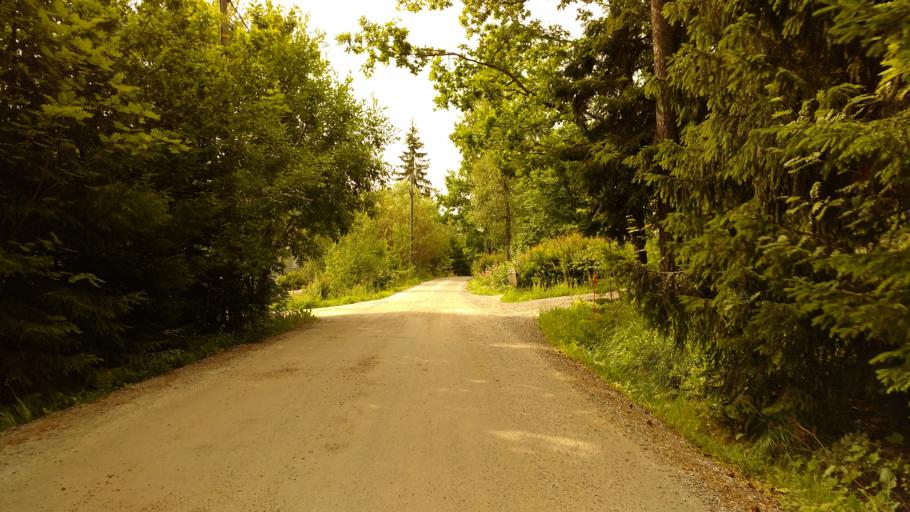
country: FI
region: Varsinais-Suomi
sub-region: Turku
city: Kaarina
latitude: 60.4454
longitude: 22.4218
